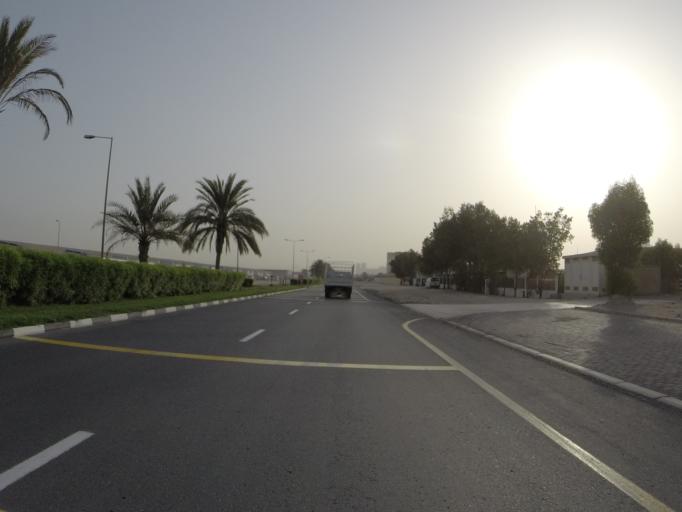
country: AE
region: Dubai
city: Dubai
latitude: 24.9629
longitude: 55.0680
